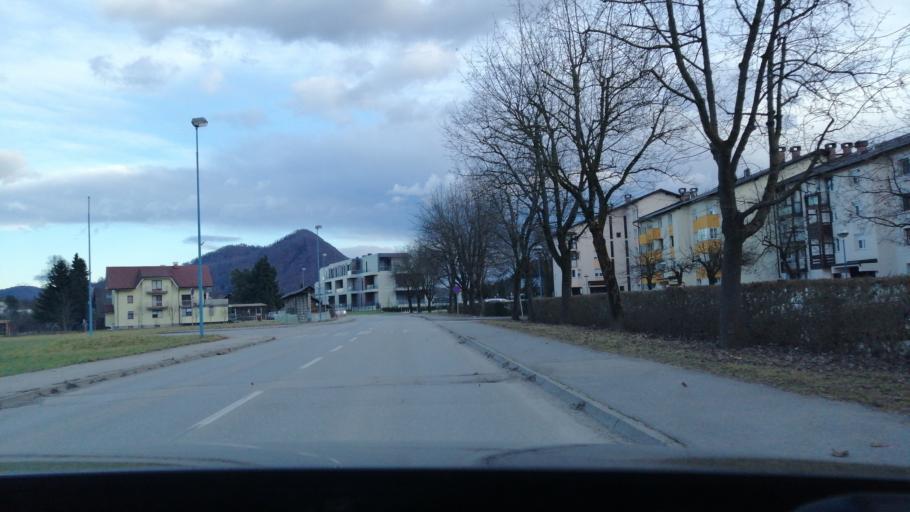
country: SI
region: Medvode
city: Medvode
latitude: 46.1343
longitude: 14.4134
